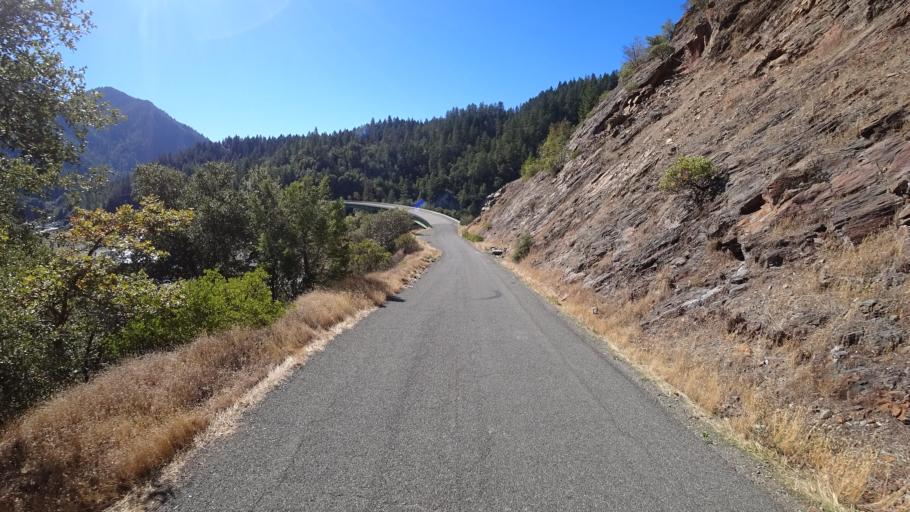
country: US
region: California
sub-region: Siskiyou County
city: Happy Camp
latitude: 41.3791
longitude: -123.4934
